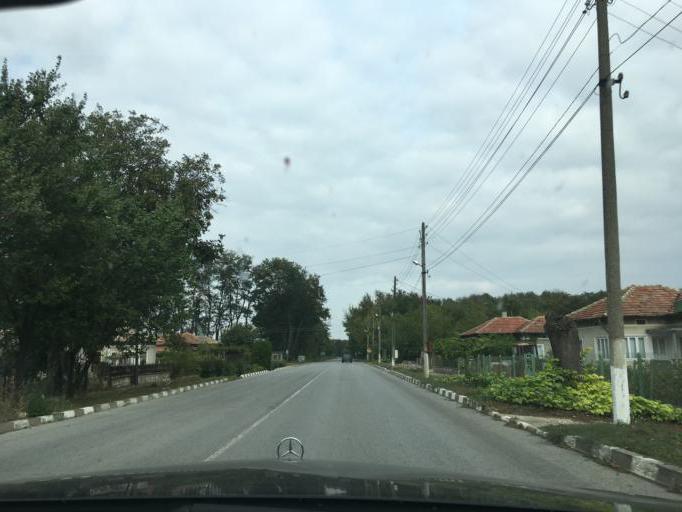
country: RO
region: Constanta
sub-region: Comuna Cerchezu
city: Cerchezu
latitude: 43.7570
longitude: 28.1133
